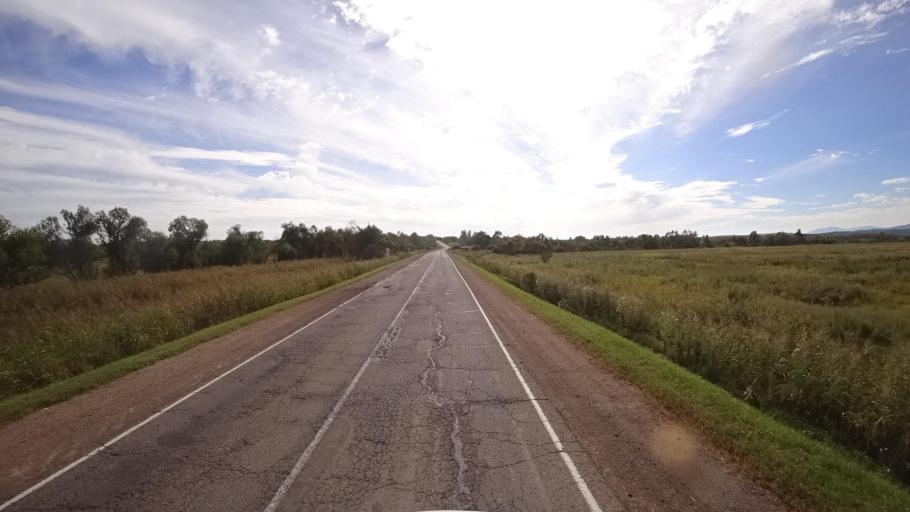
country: RU
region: Primorskiy
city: Dostoyevka
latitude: 44.3124
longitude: 133.4587
